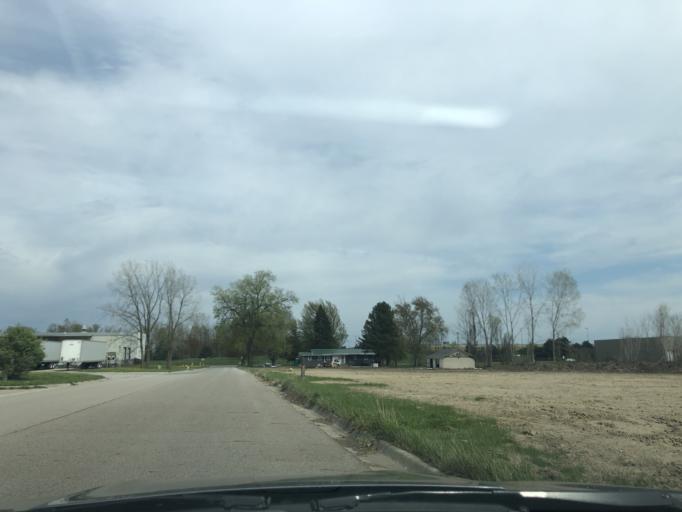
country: US
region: Michigan
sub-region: Eaton County
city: Waverly
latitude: 42.7035
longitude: -84.6454
